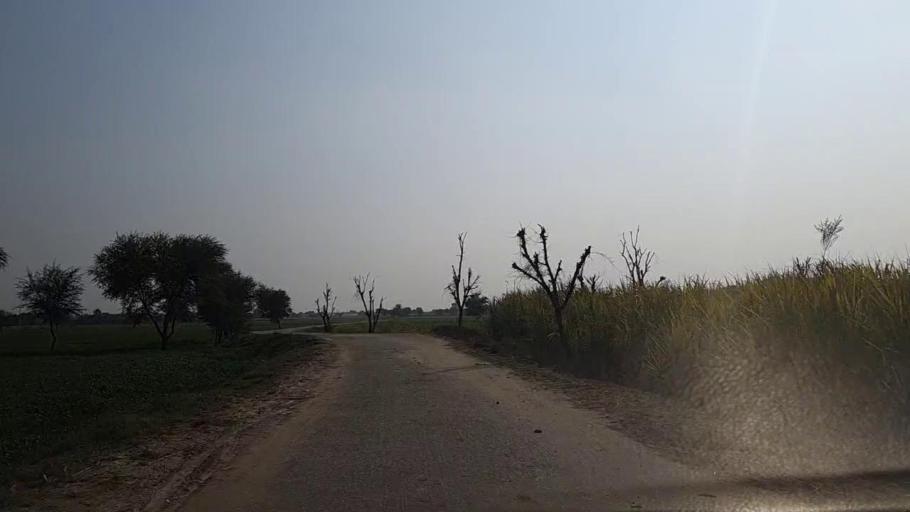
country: PK
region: Sindh
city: Daur
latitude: 26.4047
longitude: 68.4175
